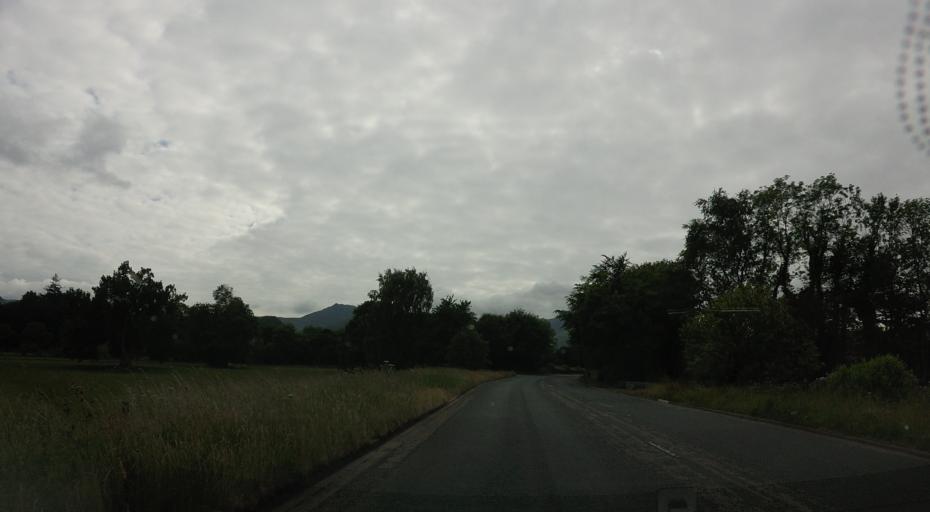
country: GB
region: England
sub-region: Cumbria
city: Keswick
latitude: 54.6059
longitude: -3.1530
